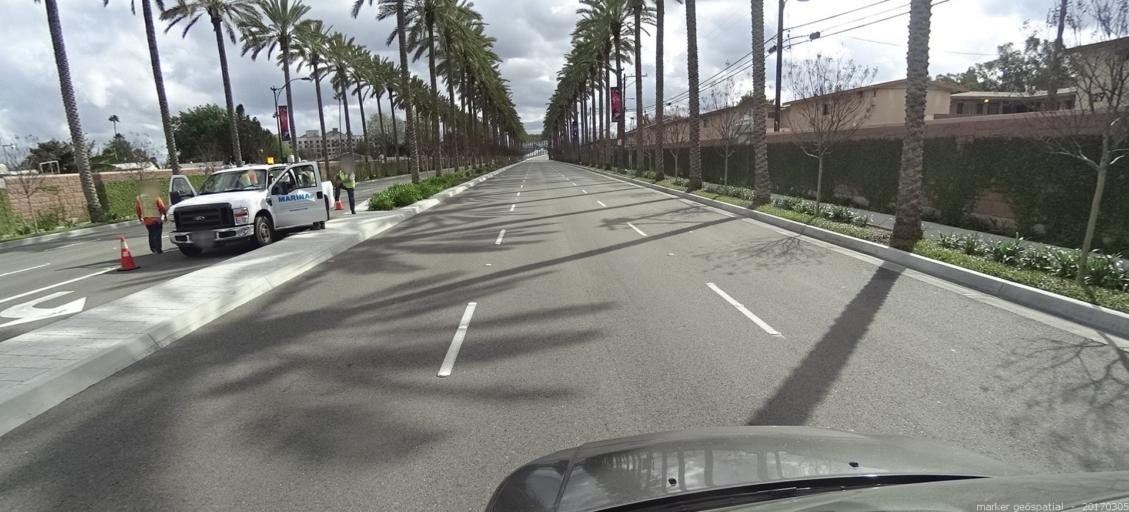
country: US
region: California
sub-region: Orange County
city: Anaheim
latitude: 33.7998
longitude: -117.9055
